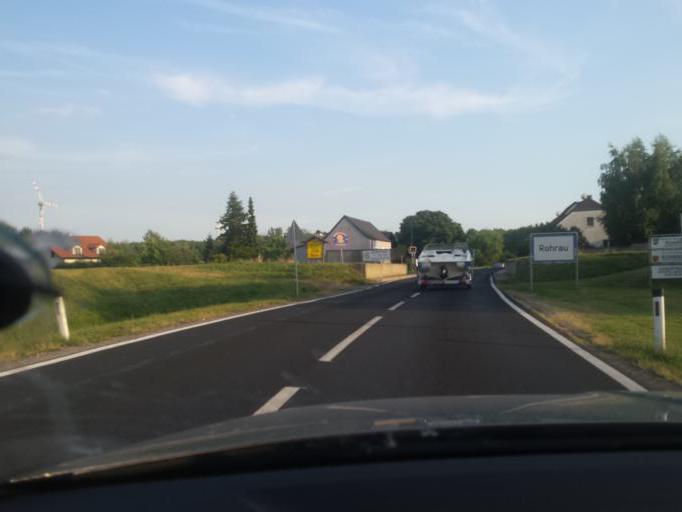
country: AT
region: Lower Austria
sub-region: Politischer Bezirk Bruck an der Leitha
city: Rohrau
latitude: 48.0702
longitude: 16.8641
